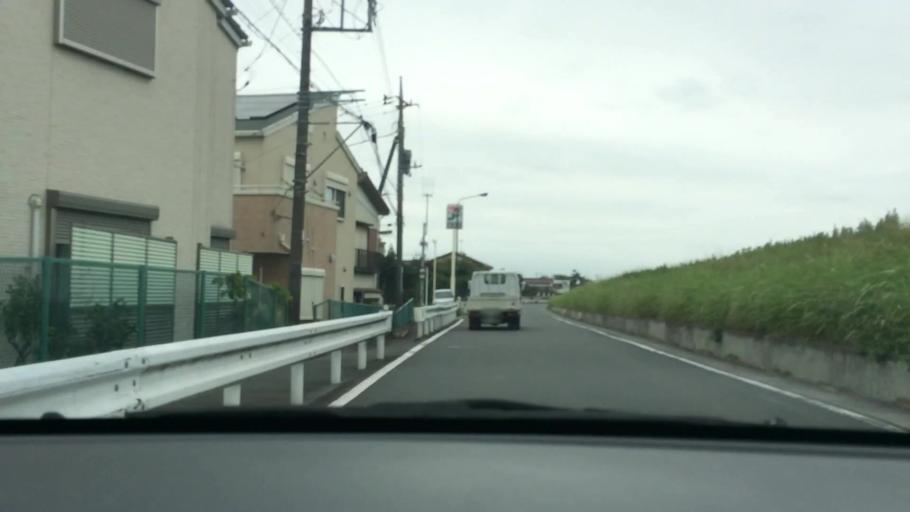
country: JP
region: Chiba
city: Matsudo
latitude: 35.7909
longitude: 139.8869
